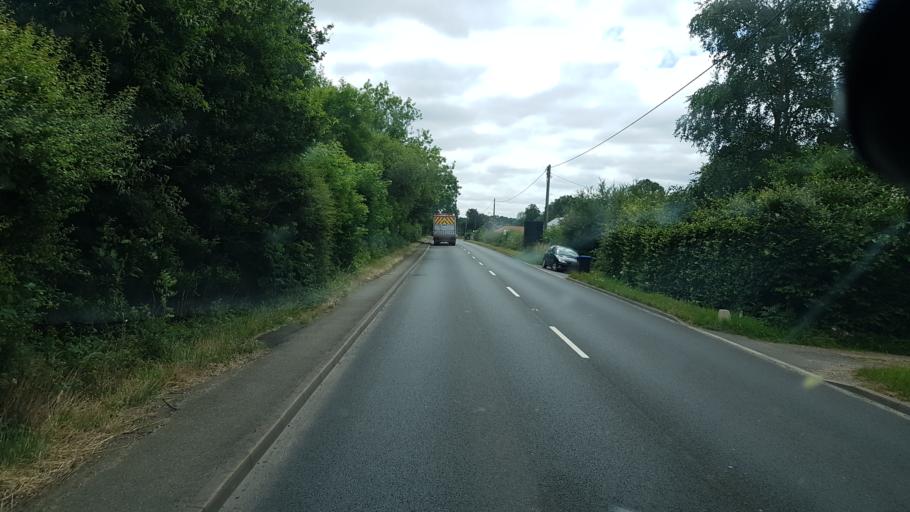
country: GB
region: England
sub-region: Surrey
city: Lingfield
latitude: 51.1872
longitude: -0.0481
